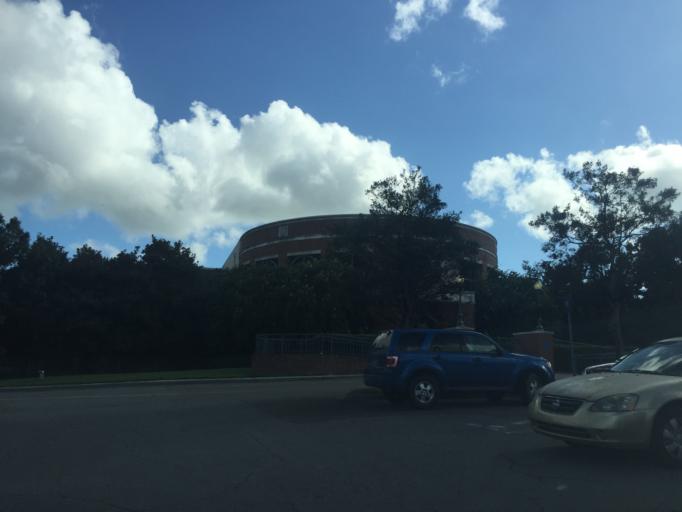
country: US
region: Georgia
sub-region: Chatham County
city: Georgetown
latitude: 31.9850
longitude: -81.1719
